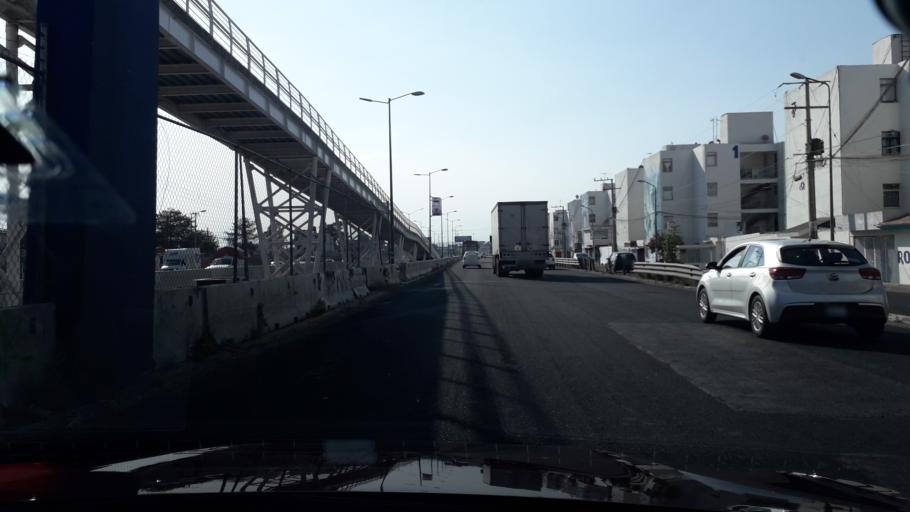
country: MX
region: Puebla
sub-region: Puebla
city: El Capulo (La Quebradora)
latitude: 18.9864
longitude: -98.2348
